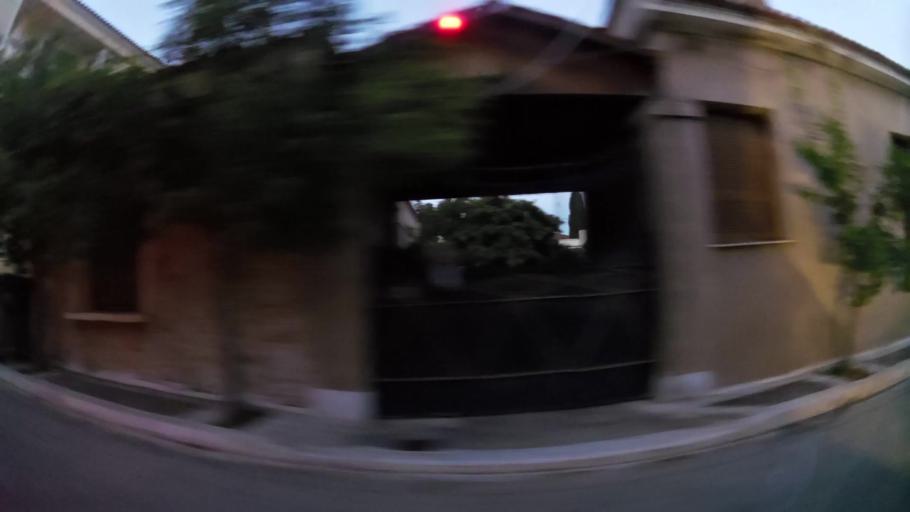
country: GR
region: Attica
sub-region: Nomarchia Anatolikis Attikis
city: Paiania
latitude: 37.9565
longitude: 23.8567
